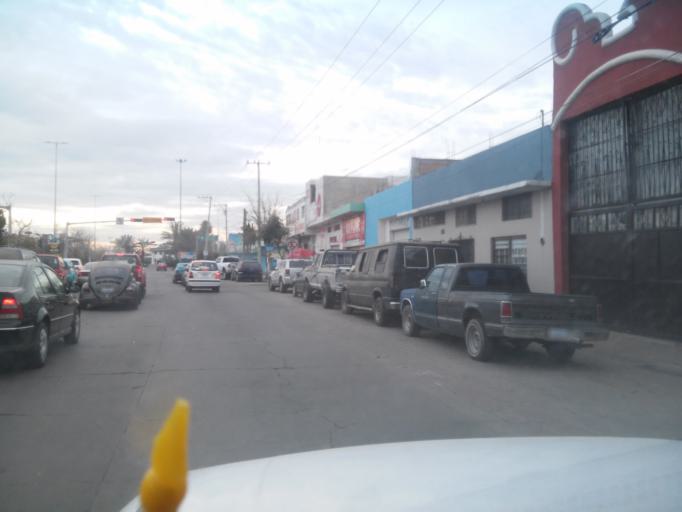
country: MX
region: Durango
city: Victoria de Durango
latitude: 24.0034
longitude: -104.6543
